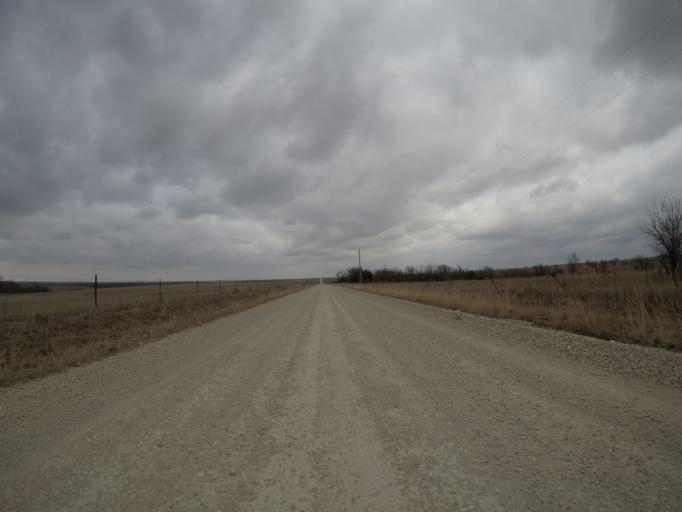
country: US
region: Kansas
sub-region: Morris County
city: Council Grove
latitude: 38.7467
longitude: -96.2797
